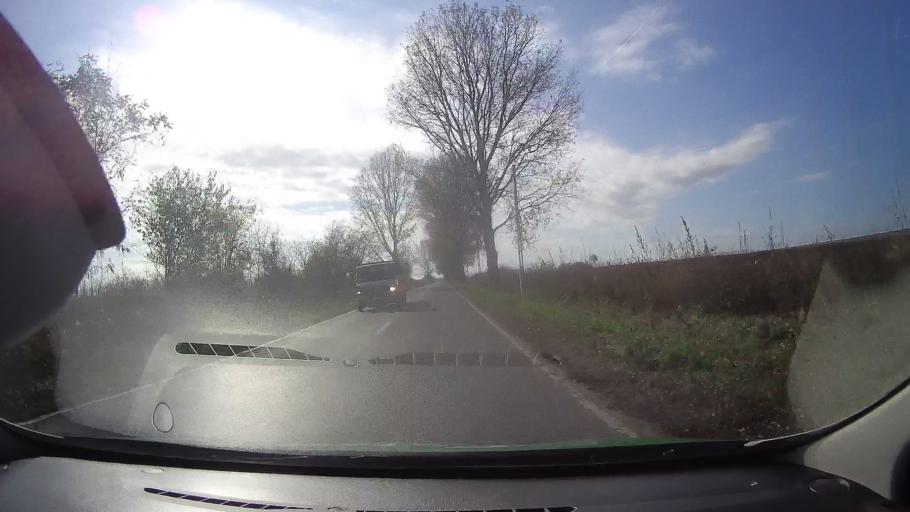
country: RO
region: Tulcea
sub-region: Comuna Valea Nucarilor
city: Agighiol
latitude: 44.9894
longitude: 28.8851
